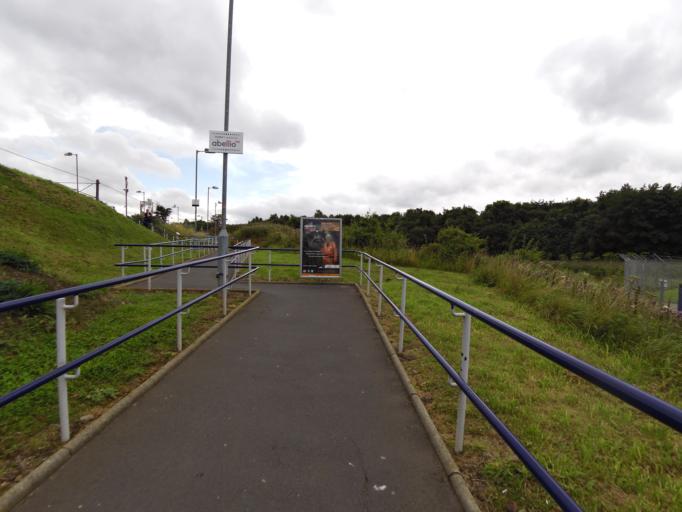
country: GB
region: Scotland
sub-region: East Lothian
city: Musselburgh
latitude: 55.9334
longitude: -3.0915
